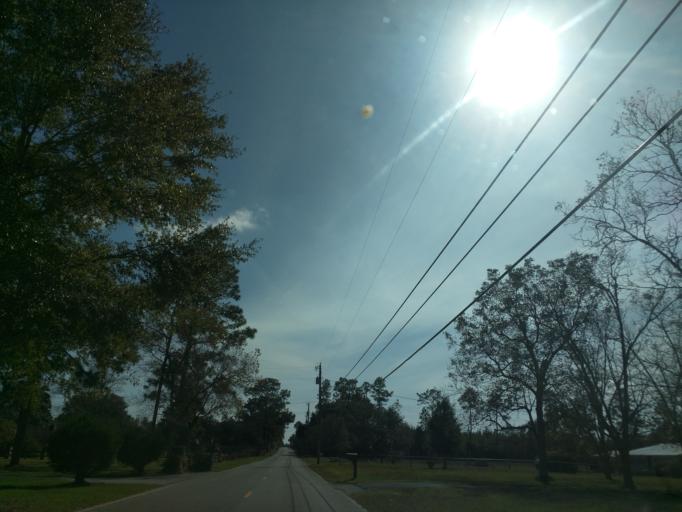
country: US
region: Florida
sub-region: Escambia County
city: Cantonment
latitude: 30.5486
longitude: -87.4057
